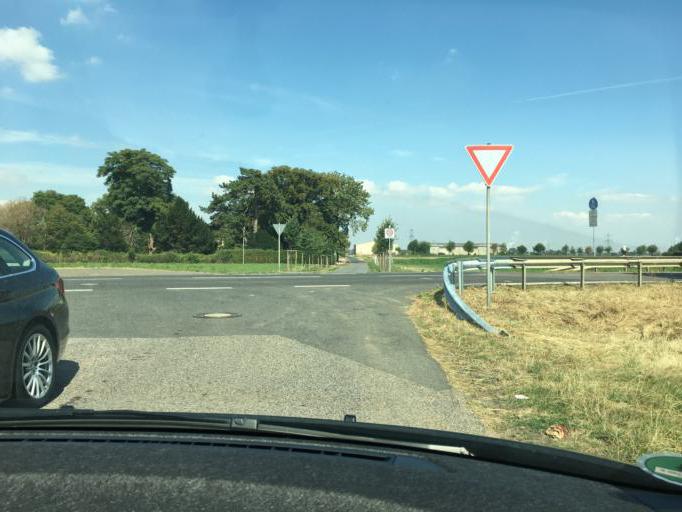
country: DE
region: North Rhine-Westphalia
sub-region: Regierungsbezirk Koln
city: Merzenich
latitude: 50.8375
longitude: 6.5860
